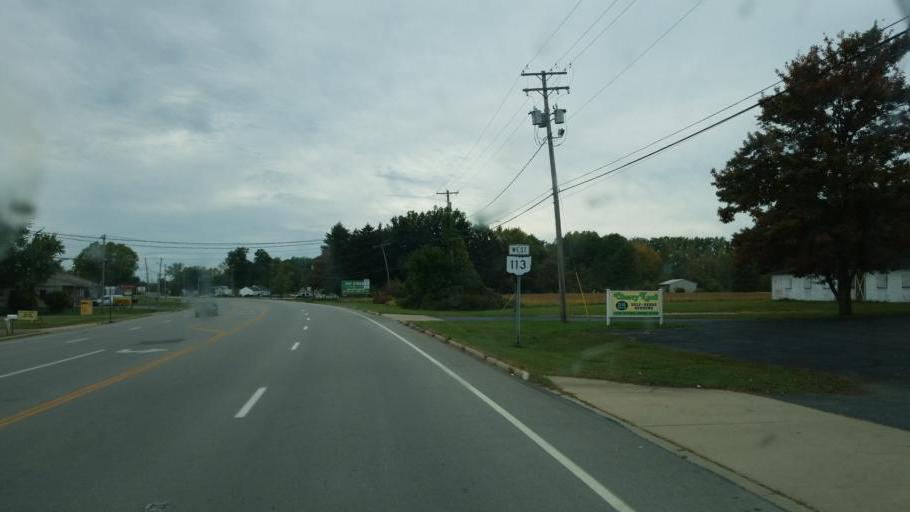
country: US
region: Ohio
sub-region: Lorain County
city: Amherst
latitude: 41.3666
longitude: -82.2114
